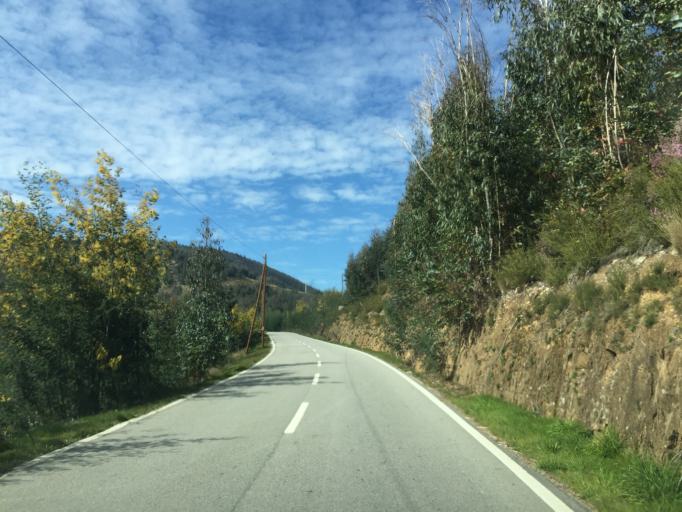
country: PT
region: Aveiro
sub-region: Arouca
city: Arouca
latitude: 40.9570
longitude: -8.1960
